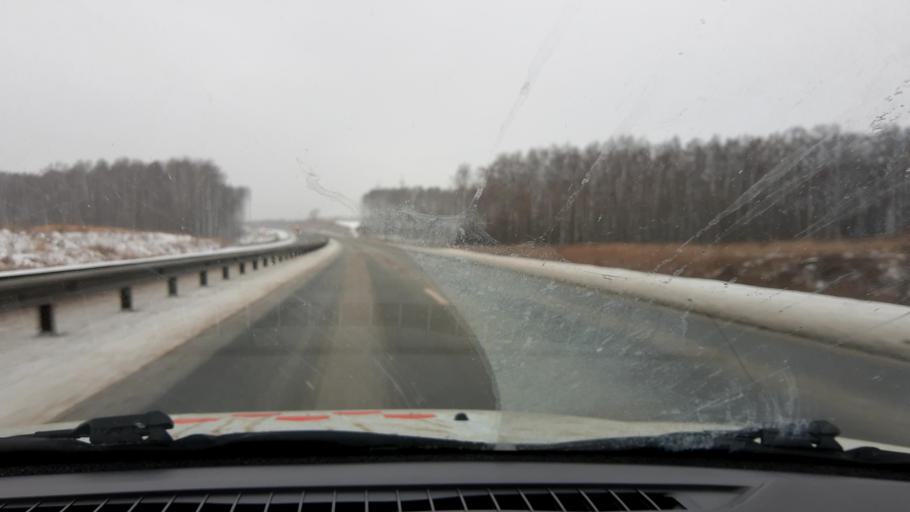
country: RU
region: Nizjnij Novgorod
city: Kstovo
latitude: 56.0985
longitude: 44.0624
